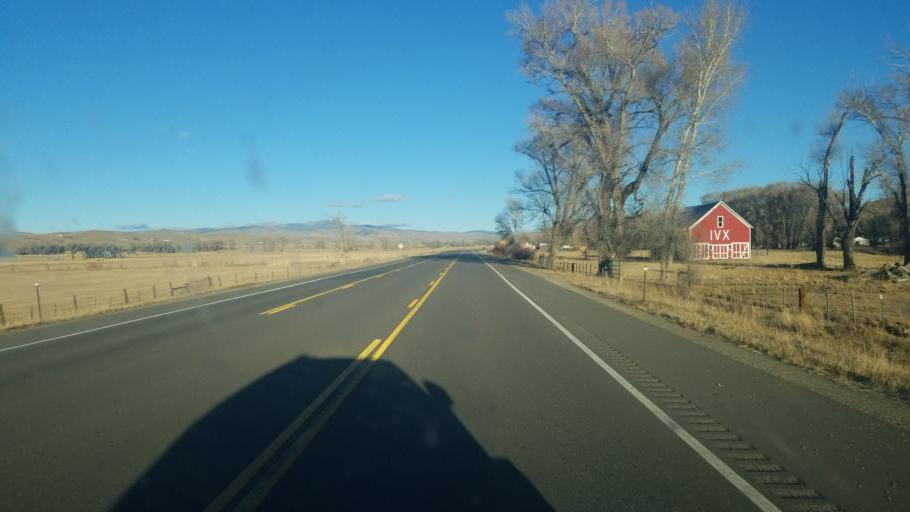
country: US
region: Colorado
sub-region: Gunnison County
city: Gunnison
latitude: 38.5218
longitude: -106.9948
